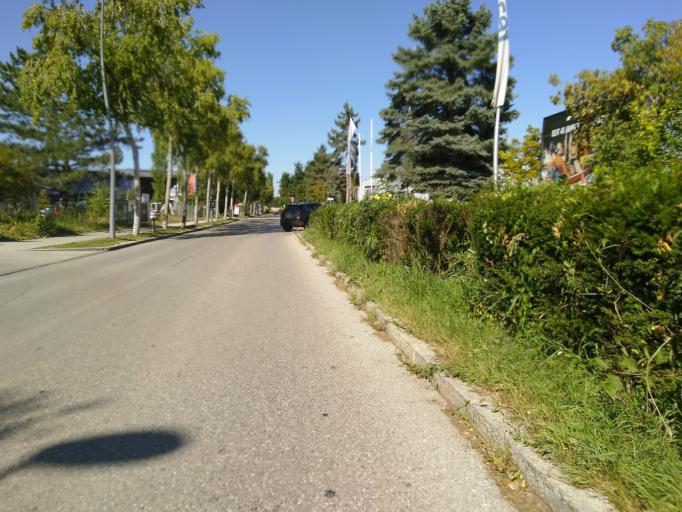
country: DE
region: Bavaria
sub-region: Upper Bavaria
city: Bogenhausen
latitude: 48.1935
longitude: 11.5965
